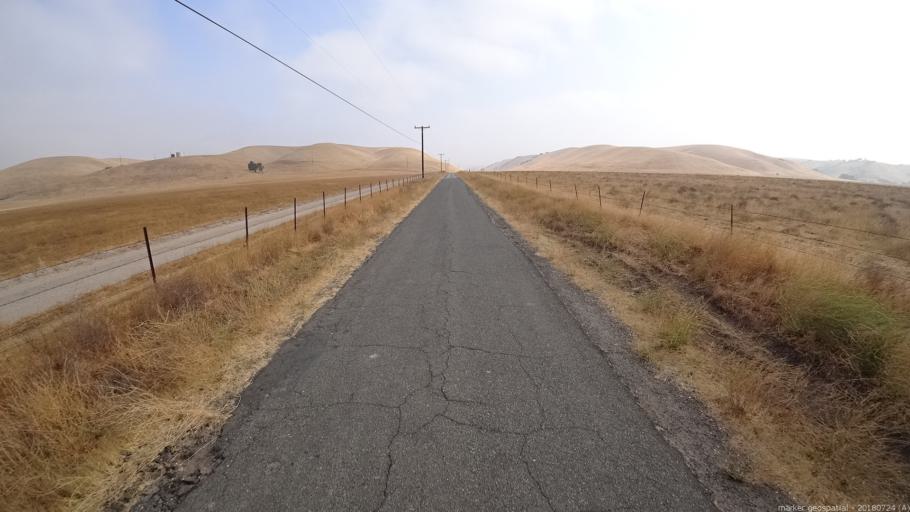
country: US
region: California
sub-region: San Luis Obispo County
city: San Miguel
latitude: 35.8677
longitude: -120.7956
